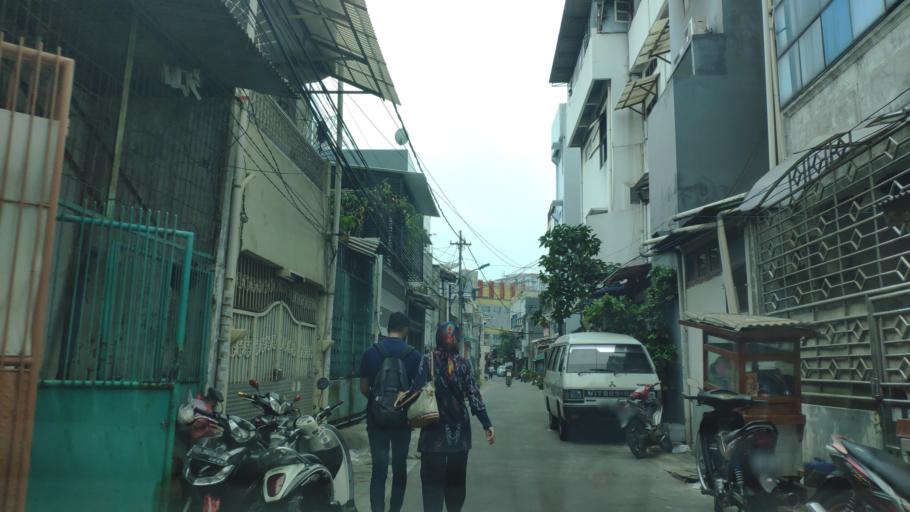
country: ID
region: Jakarta Raya
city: Jakarta
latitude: -6.1443
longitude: 106.8140
